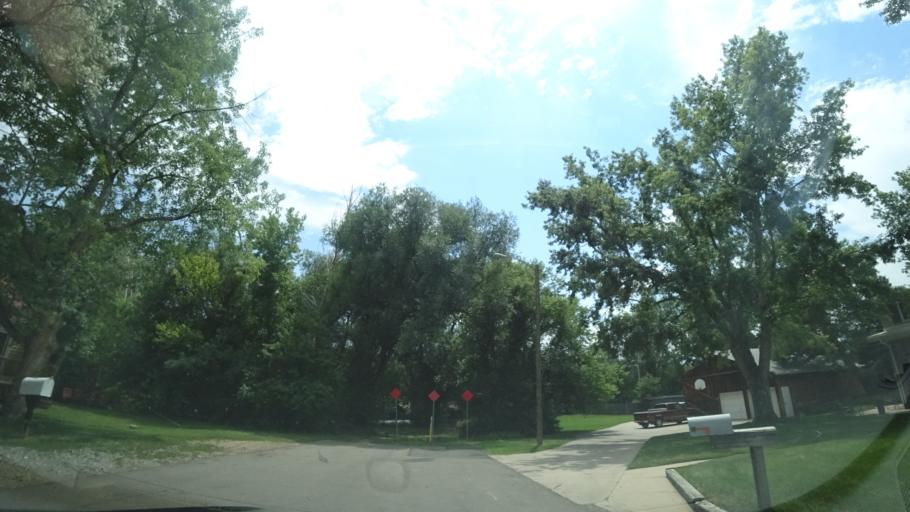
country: US
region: Colorado
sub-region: Jefferson County
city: Lakewood
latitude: 39.7192
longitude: -105.0857
